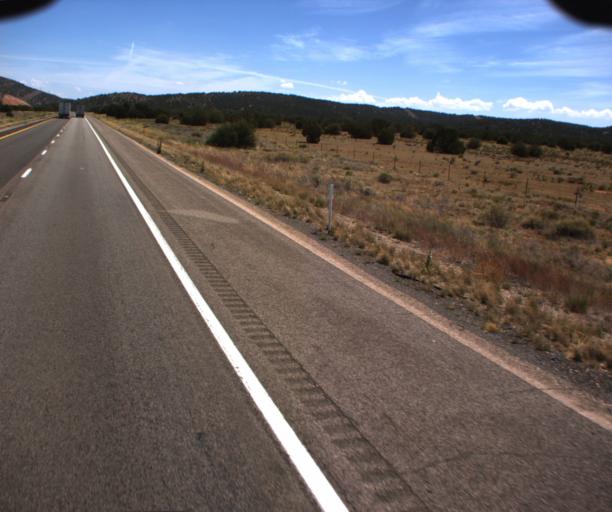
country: US
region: Arizona
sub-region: Mohave County
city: Peach Springs
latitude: 35.2727
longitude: -113.1400
